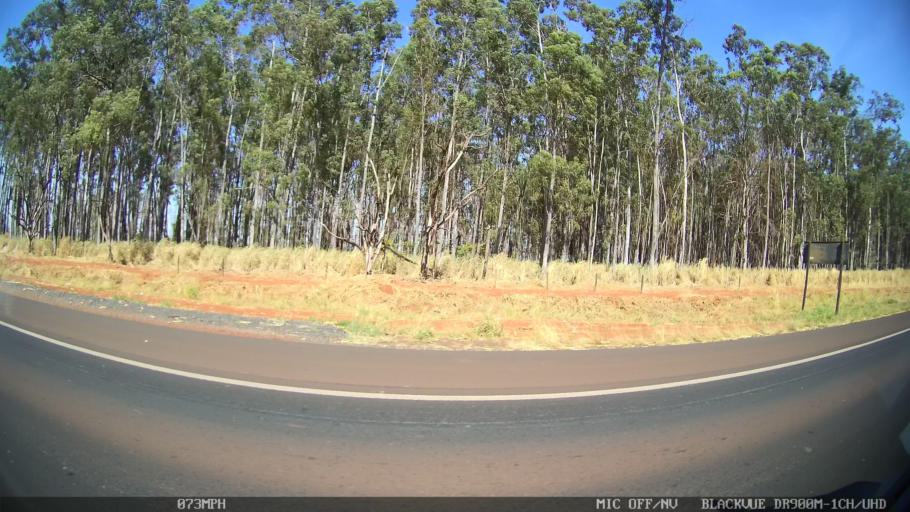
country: BR
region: Sao Paulo
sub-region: Barretos
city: Barretos
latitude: -20.4919
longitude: -48.5243
